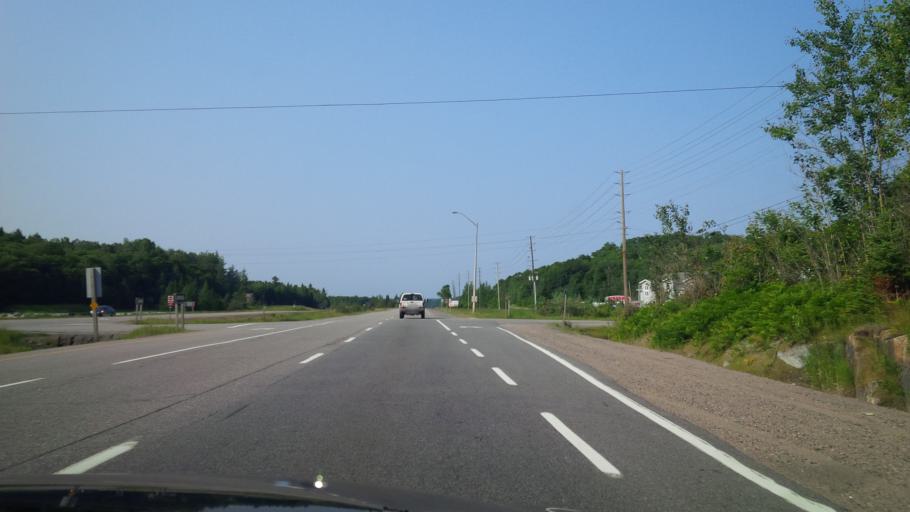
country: CA
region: Ontario
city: Huntsville
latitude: 45.2766
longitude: -79.2806
